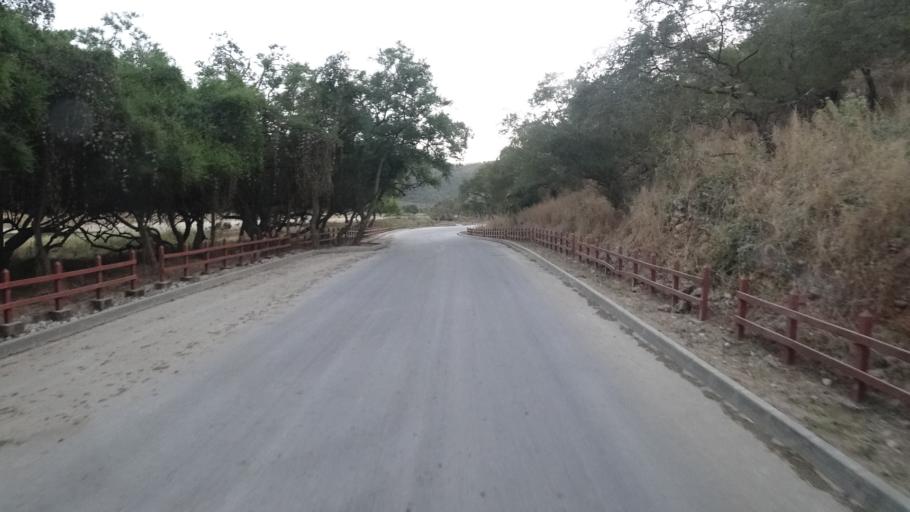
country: OM
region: Zufar
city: Salalah
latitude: 17.0955
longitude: 54.4489
